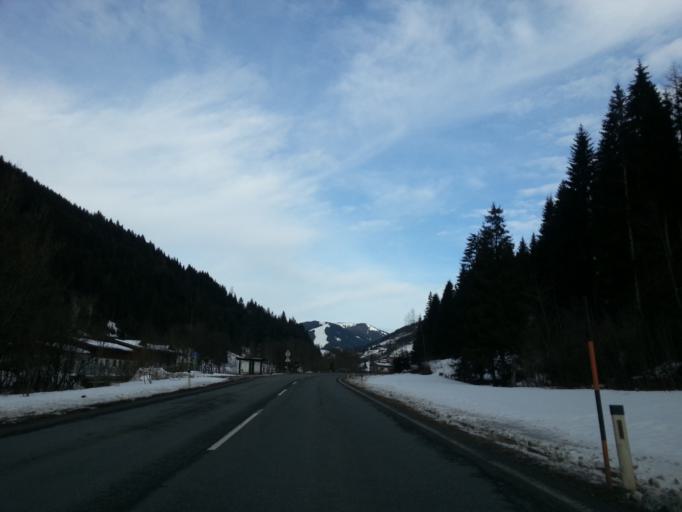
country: AT
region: Salzburg
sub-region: Politischer Bezirk Zell am See
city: Viehhofen
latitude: 47.3720
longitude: 12.6937
